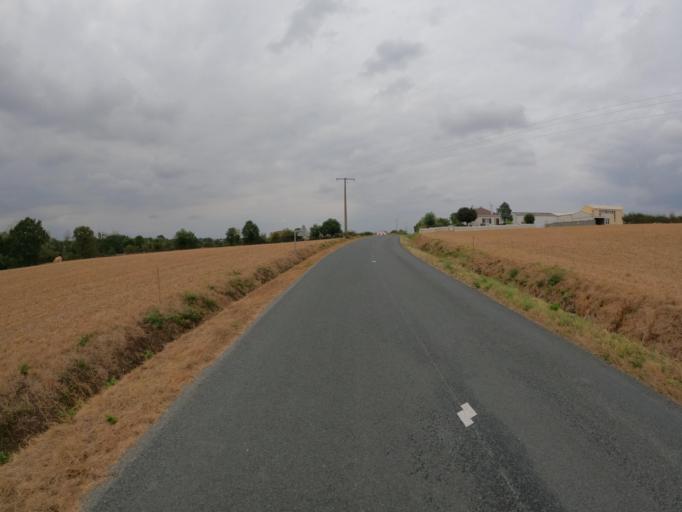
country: FR
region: Pays de la Loire
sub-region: Departement de la Vendee
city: Les Landes-Genusson
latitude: 46.9790
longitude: -1.1126
